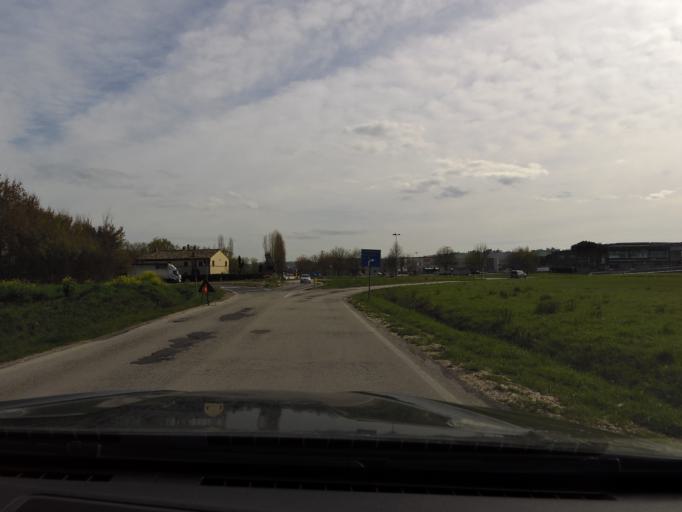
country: IT
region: The Marches
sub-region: Provincia di Ancona
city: Camerano
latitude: 43.5171
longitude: 13.5301
